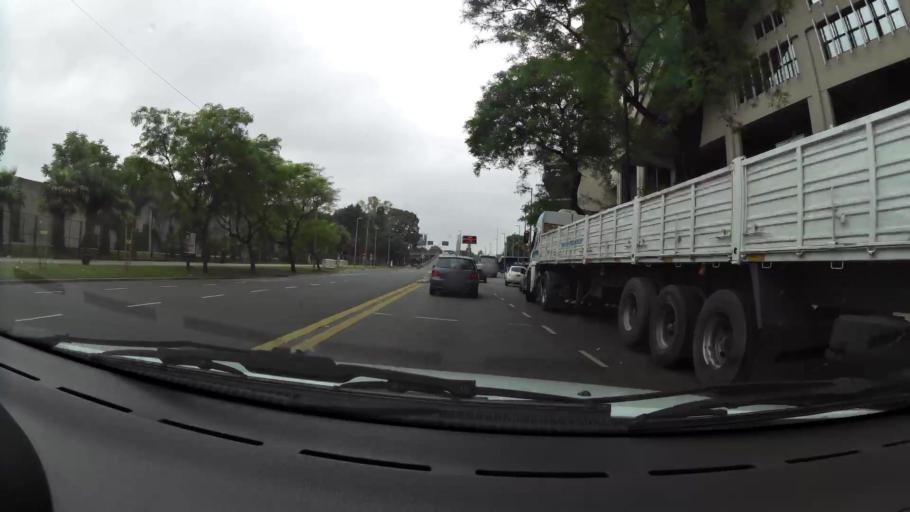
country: AR
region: Buenos Aires F.D.
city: Colegiales
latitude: -34.5447
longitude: -58.4509
